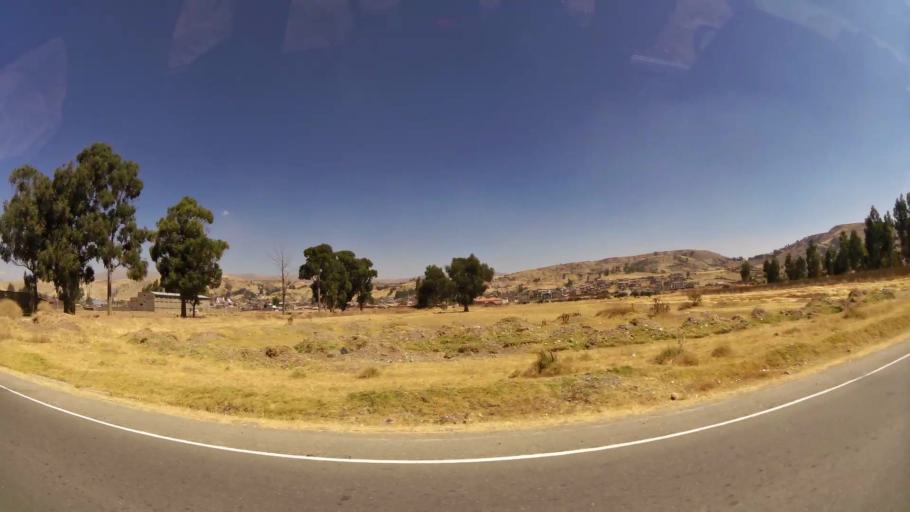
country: PE
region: Junin
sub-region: Provincia de Jauja
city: Jauja
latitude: -11.7656
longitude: -75.4945
